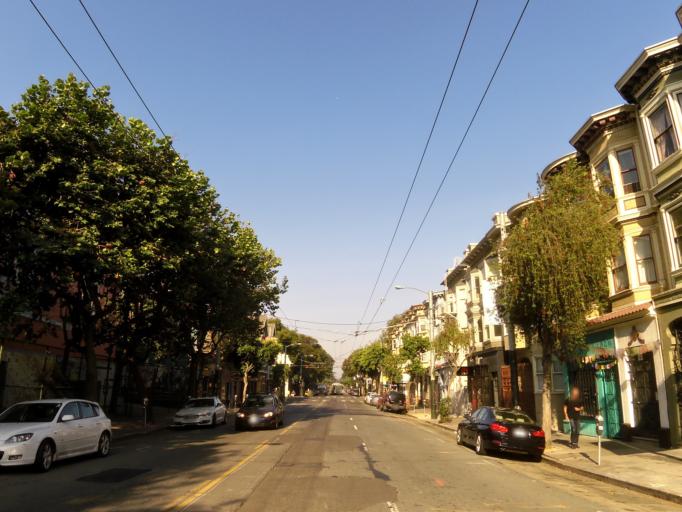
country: US
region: California
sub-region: San Francisco County
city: San Francisco
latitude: 37.7704
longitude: -122.4443
